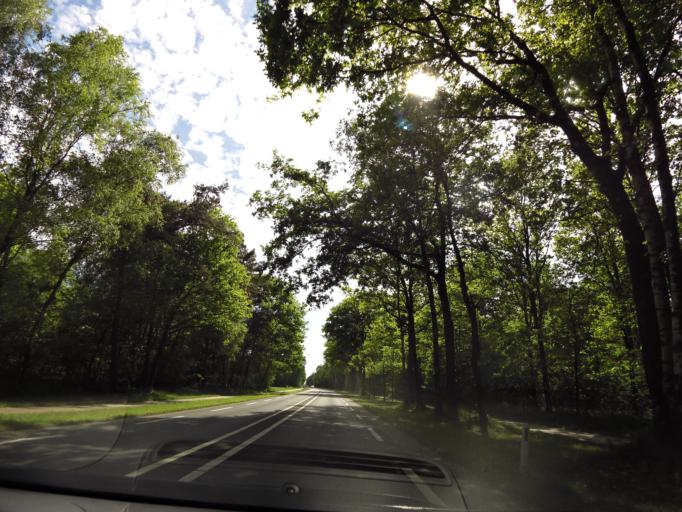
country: DE
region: North Rhine-Westphalia
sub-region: Regierungsbezirk Koln
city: Waldfeucht
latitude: 51.0909
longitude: 5.9926
